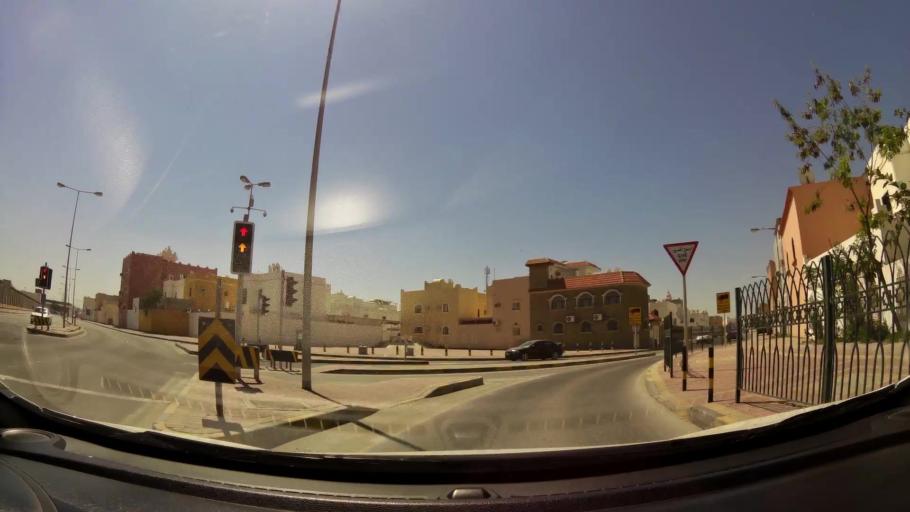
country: BH
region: Muharraq
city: Al Muharraq
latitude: 26.2759
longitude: 50.6121
